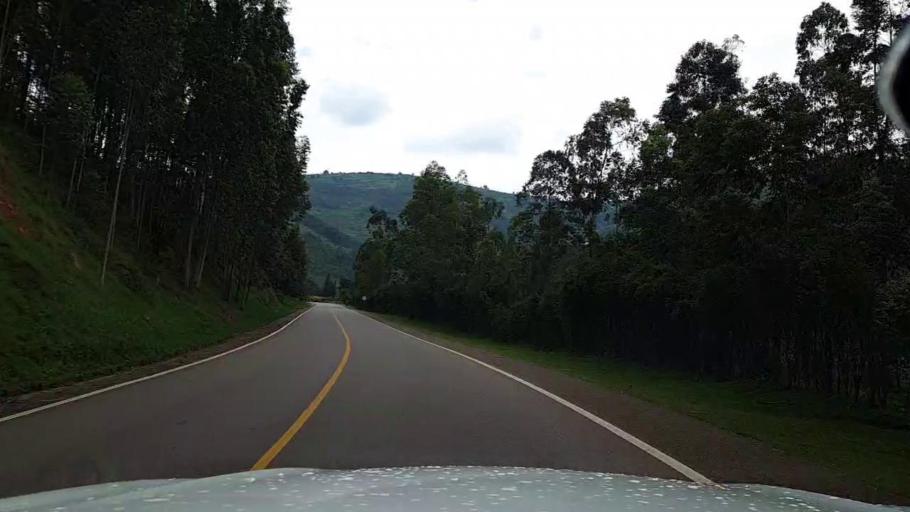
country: RW
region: Northern Province
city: Byumba
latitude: -1.7158
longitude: 30.1225
